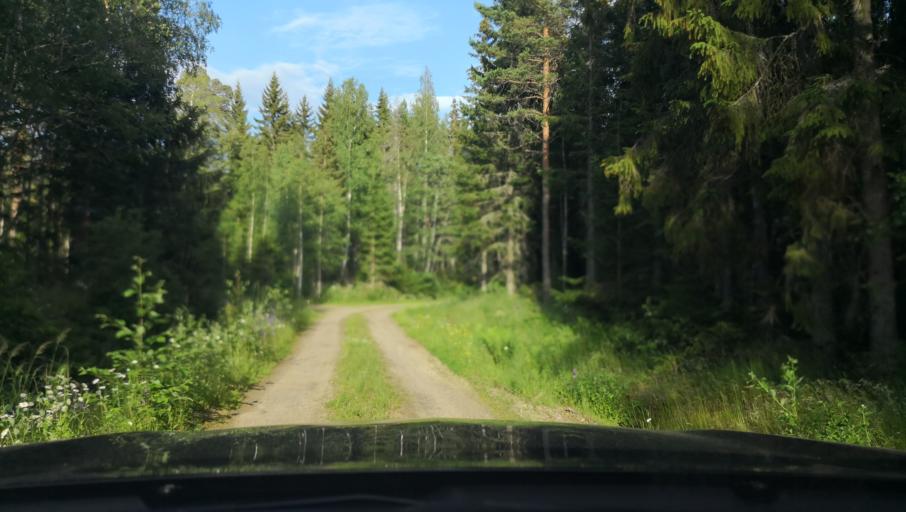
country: SE
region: Dalarna
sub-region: Ludvika Kommun
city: Ludvika
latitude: 60.0758
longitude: 15.2881
